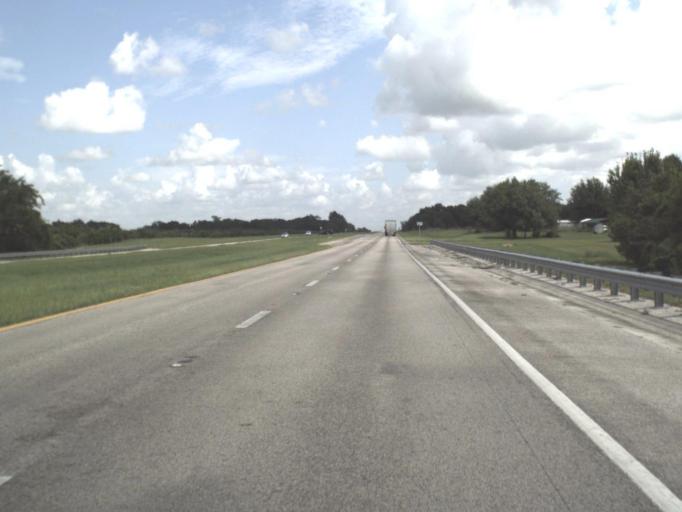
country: US
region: Florida
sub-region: DeSoto County
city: Arcadia
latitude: 27.2873
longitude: -81.8284
